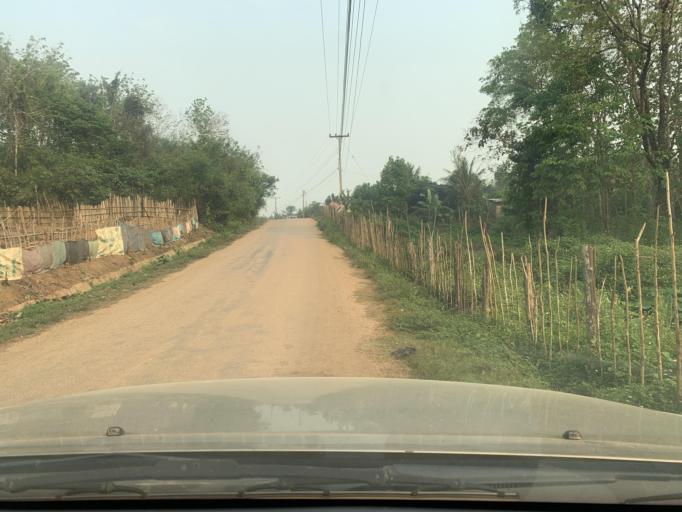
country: LA
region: Louangphabang
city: Louangphabang
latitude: 19.9131
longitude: 102.0774
